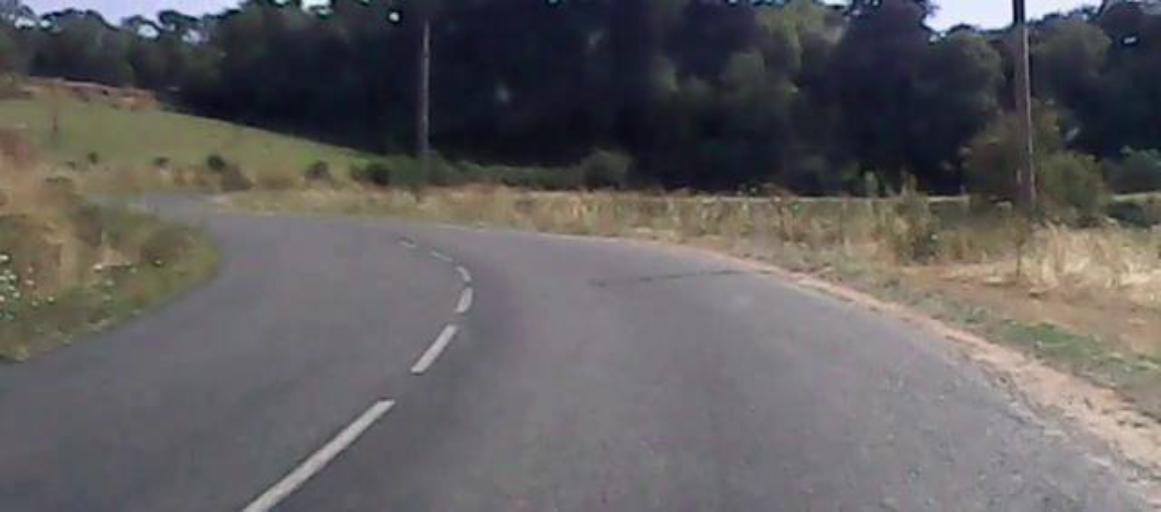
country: FR
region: Auvergne
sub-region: Departement de l'Allier
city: Saint-Yorre
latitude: 46.0619
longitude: 3.5045
